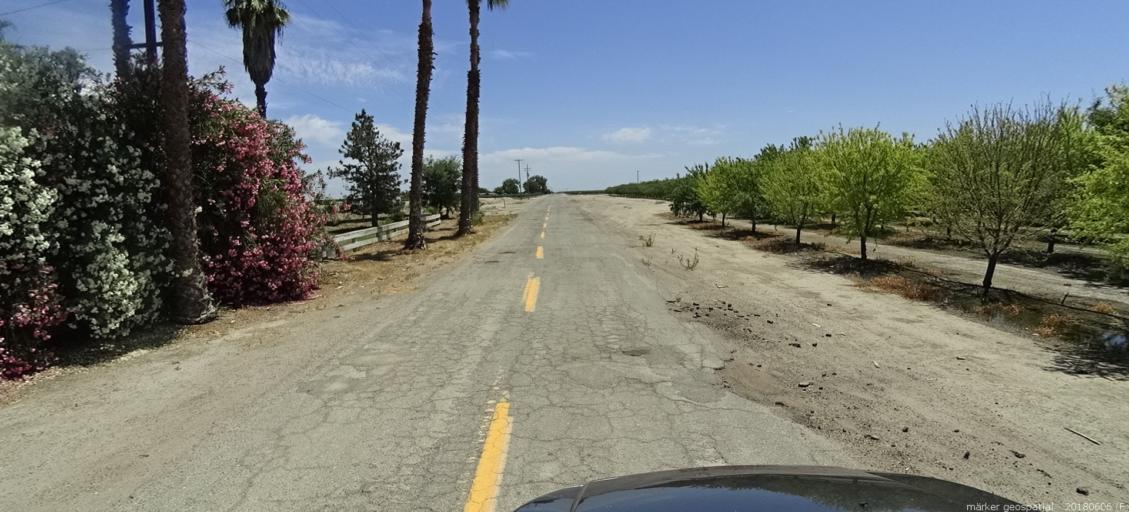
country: US
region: California
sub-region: Fresno County
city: Firebaugh
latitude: 36.8367
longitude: -120.3979
